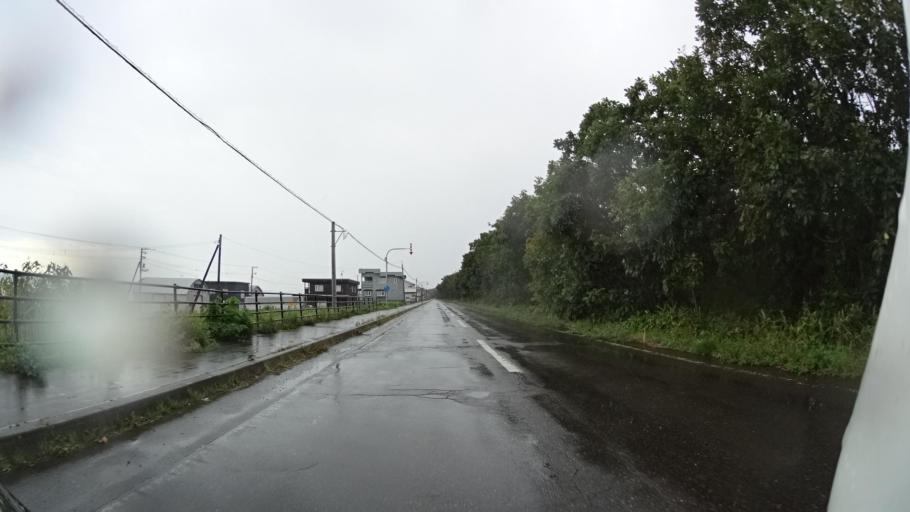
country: JP
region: Hokkaido
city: Mombetsu
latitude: 44.3328
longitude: 143.4890
